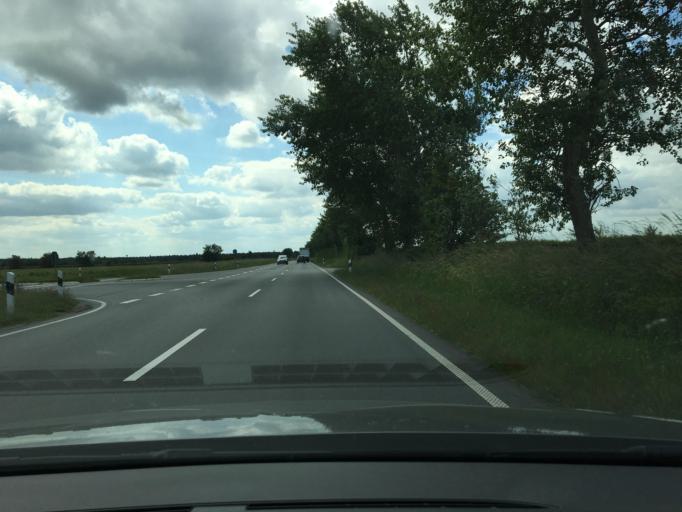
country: DE
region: Schleswig-Holstein
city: Klein Rheide
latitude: 54.4416
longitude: 9.4810
